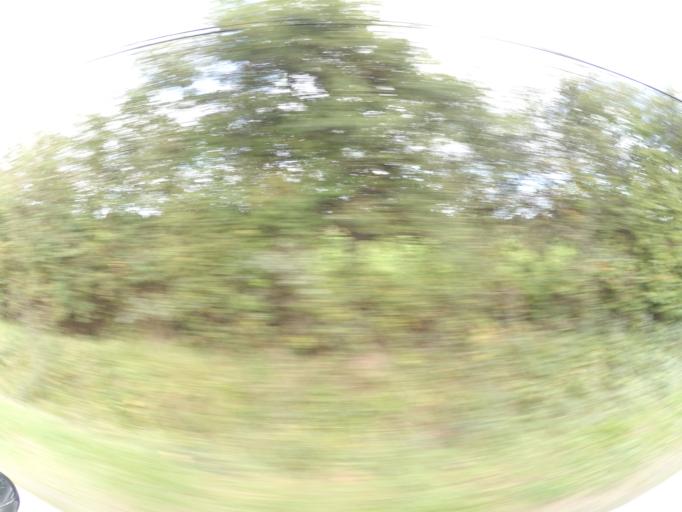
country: FR
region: Pays de la Loire
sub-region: Departement de la Loire-Atlantique
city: Fay-de-Bretagne
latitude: 47.4243
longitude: -1.7973
